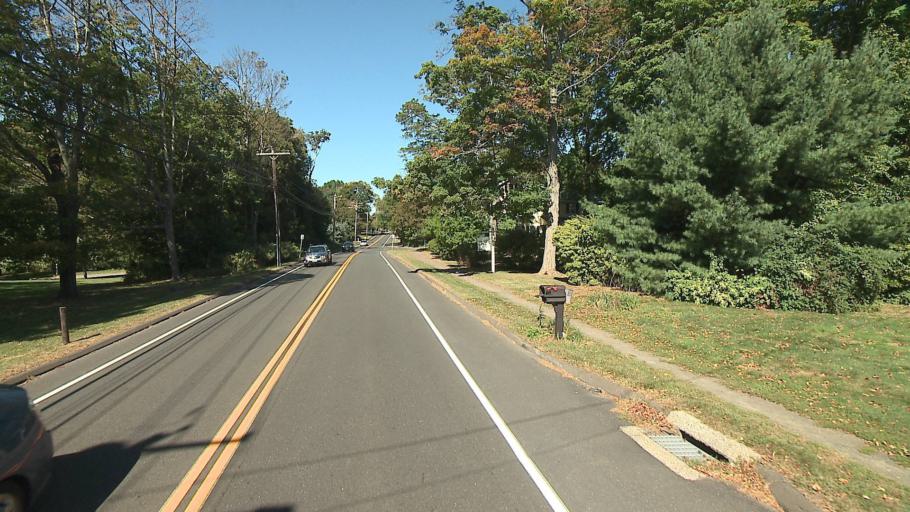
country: US
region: Connecticut
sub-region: New Haven County
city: Orange
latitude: 41.2753
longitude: -73.0239
